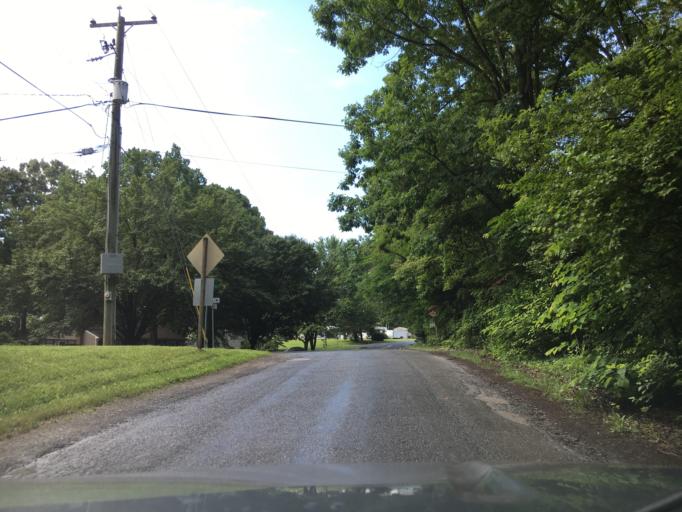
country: US
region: Virginia
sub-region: Bedford County
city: Forest
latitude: 37.3633
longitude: -79.2649
